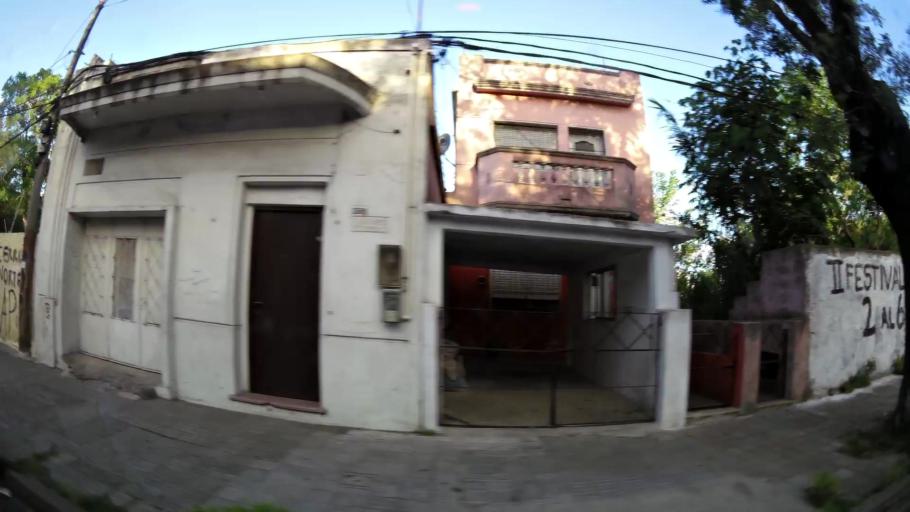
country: UY
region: Montevideo
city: Montevideo
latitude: -34.8797
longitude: -56.2502
